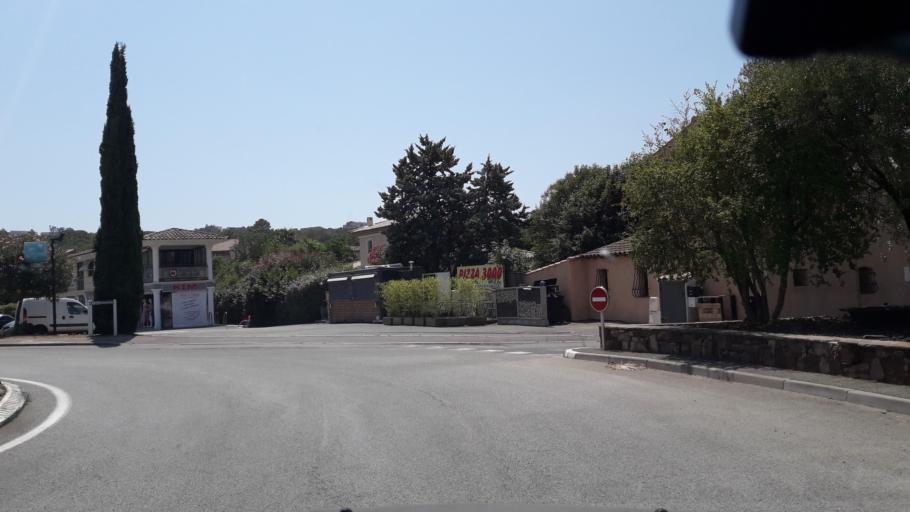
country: FR
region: Provence-Alpes-Cote d'Azur
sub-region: Departement du Var
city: Saint-Raphael
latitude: 43.4382
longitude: 6.7834
